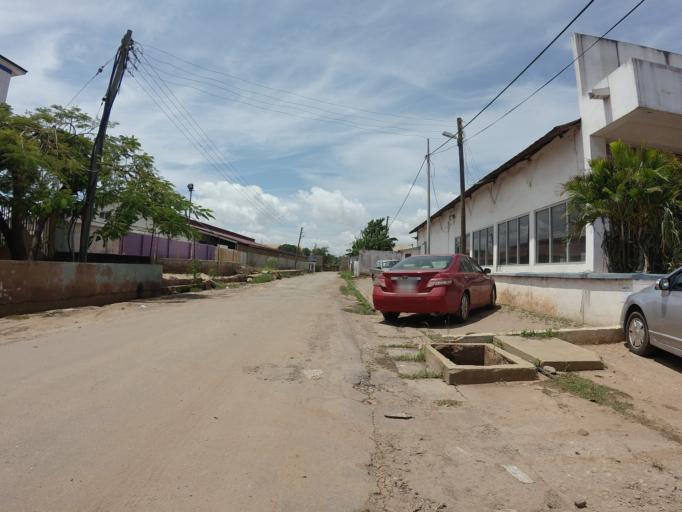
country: GH
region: Greater Accra
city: Accra
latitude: 5.5635
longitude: -0.2280
